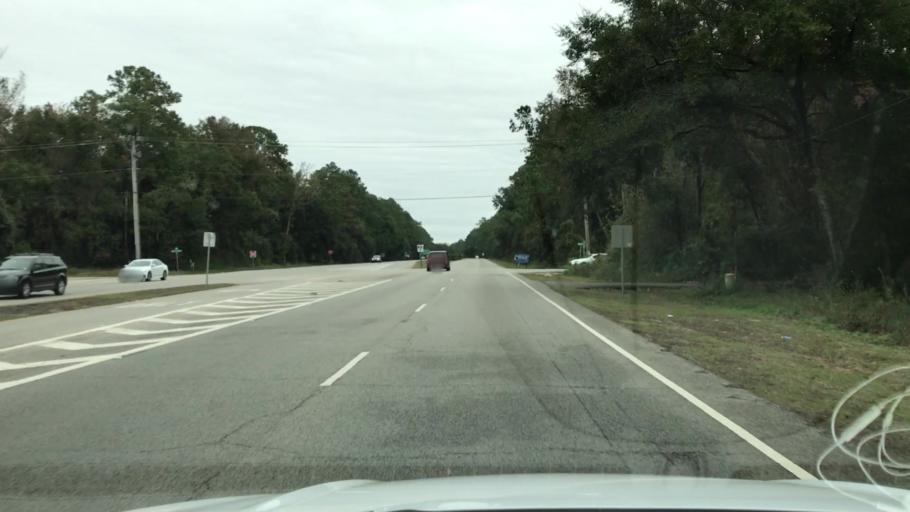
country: US
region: South Carolina
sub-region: Georgetown County
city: Murrells Inlet
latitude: 33.4957
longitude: -79.0865
